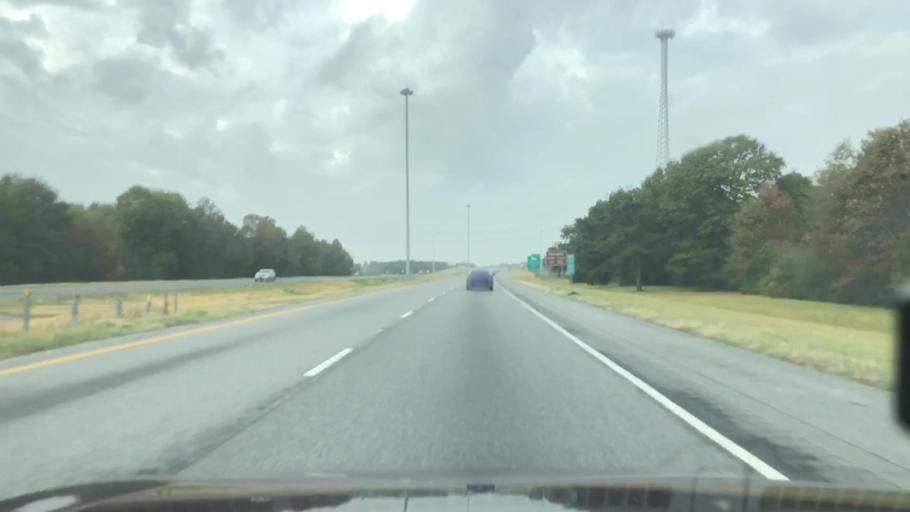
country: US
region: Louisiana
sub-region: Richland Parish
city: Delhi
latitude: 32.4417
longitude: -91.4861
